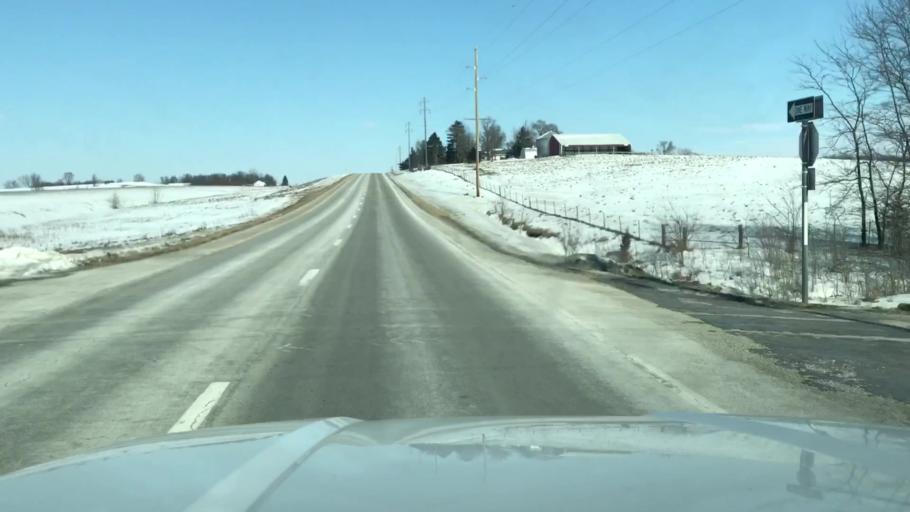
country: US
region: Missouri
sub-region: Nodaway County
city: Maryville
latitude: 40.1497
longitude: -94.8691
